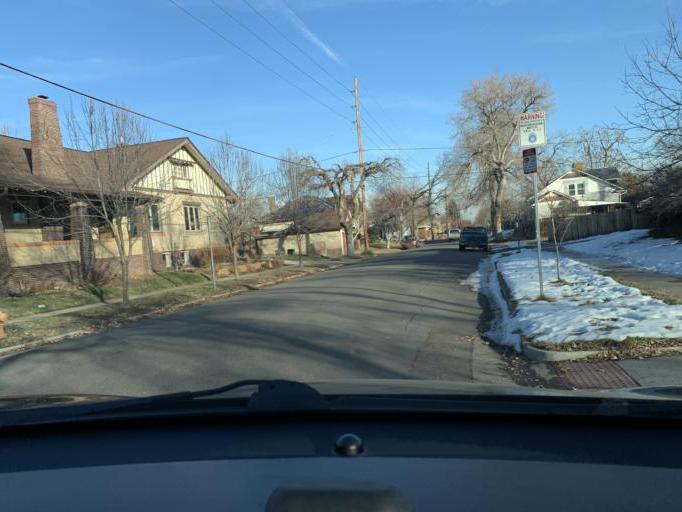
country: US
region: Colorado
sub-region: Adams County
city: Berkley
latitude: 39.7749
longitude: -105.0322
